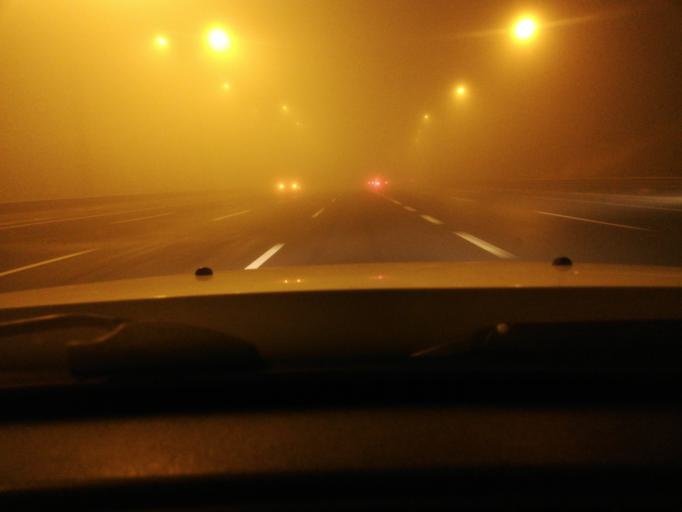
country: TR
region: Istanbul
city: Sultanbeyli
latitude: 40.9777
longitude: 29.3276
